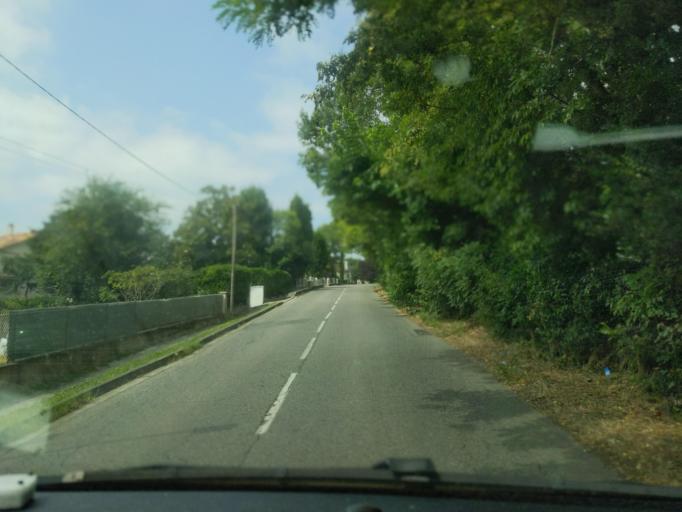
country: FR
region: Midi-Pyrenees
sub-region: Departement de la Haute-Garonne
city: Saint-Orens-de-Gameville
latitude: 43.5435
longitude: 1.5332
